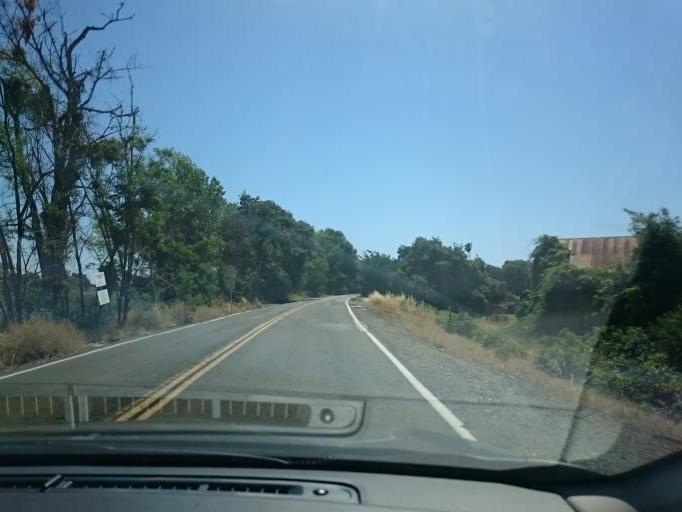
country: US
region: California
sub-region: Sacramento County
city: Parkway
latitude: 38.4732
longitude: -121.5206
